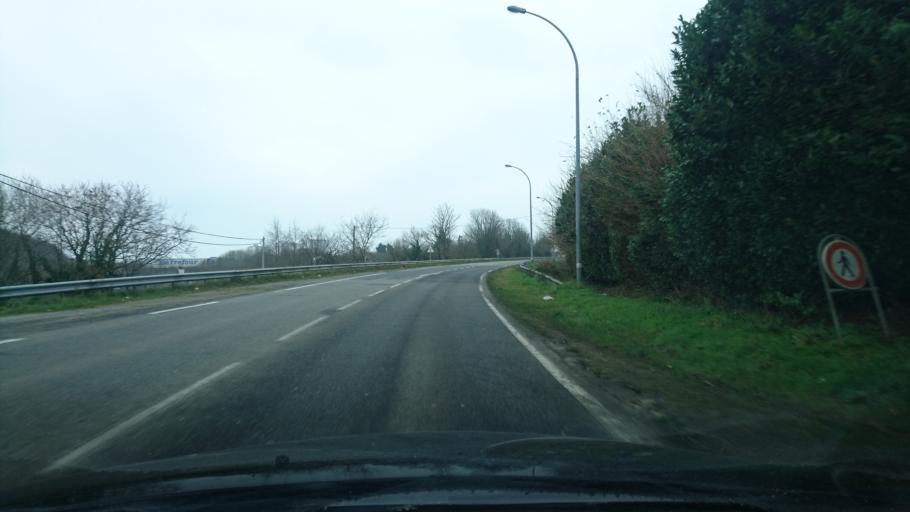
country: FR
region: Brittany
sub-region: Departement du Finistere
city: Guilers
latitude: 48.3897
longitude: -4.5327
